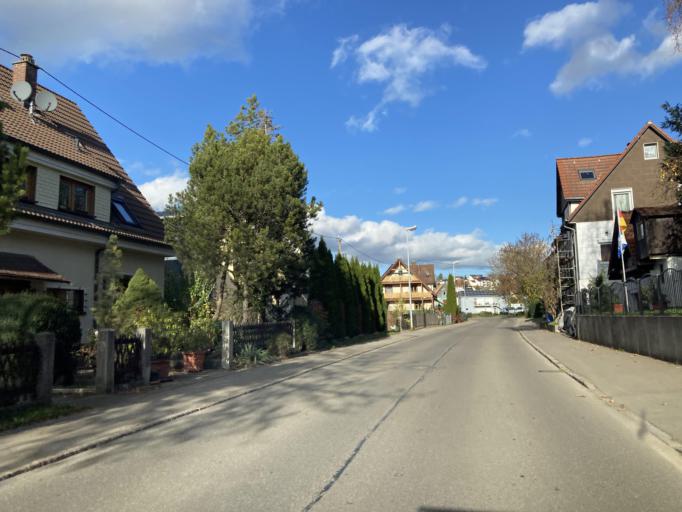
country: DE
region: Baden-Wuerttemberg
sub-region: Freiburg Region
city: Donaueschingen
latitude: 48.0025
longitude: 8.4656
